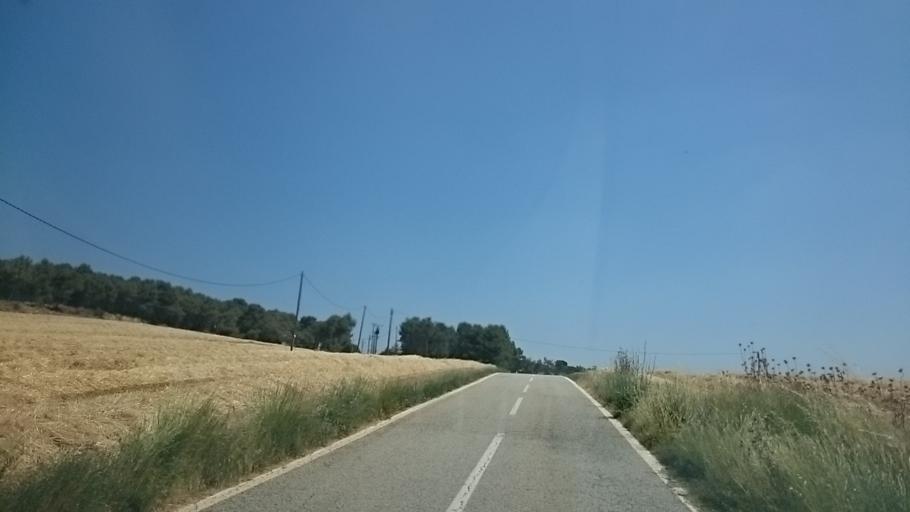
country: ES
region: Catalonia
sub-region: Provincia de Tarragona
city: Querol
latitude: 41.4532
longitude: 1.4509
